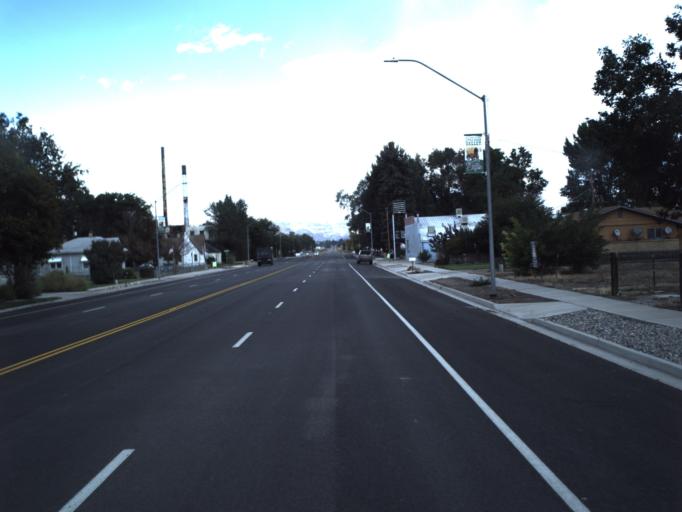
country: US
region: Utah
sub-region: Sevier County
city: Monroe
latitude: 38.6357
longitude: -112.1214
